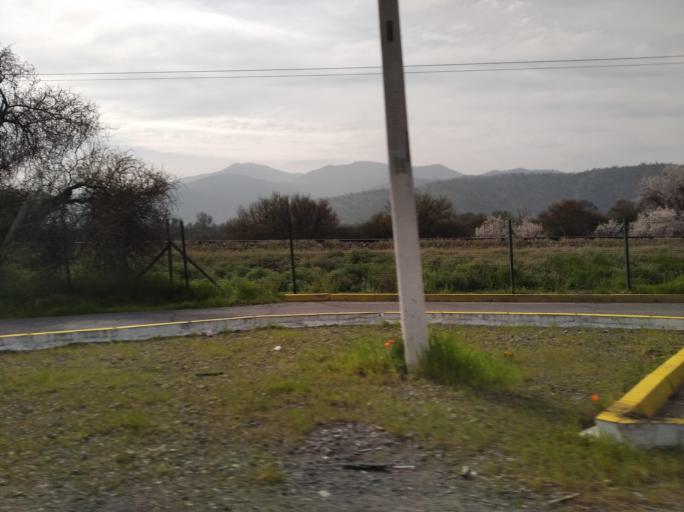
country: CL
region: Santiago Metropolitan
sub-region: Provincia de Chacabuco
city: Lampa
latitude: -33.1148
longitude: -70.9269
